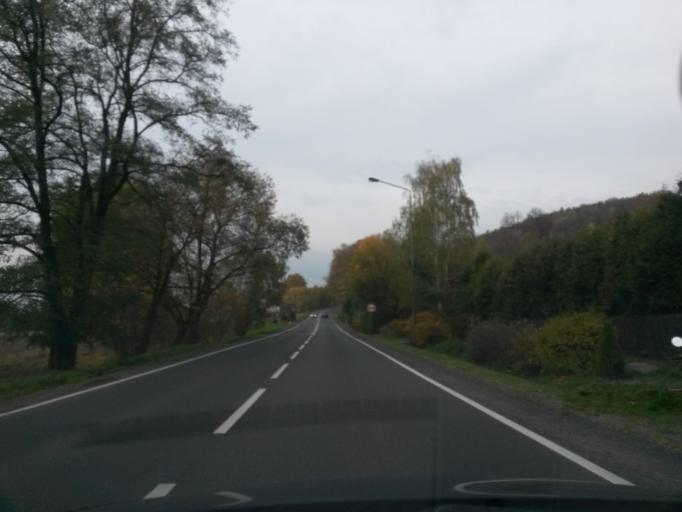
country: PL
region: Lower Silesian Voivodeship
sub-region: Powiat klodzki
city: Klodzko
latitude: 50.3782
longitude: 16.6722
